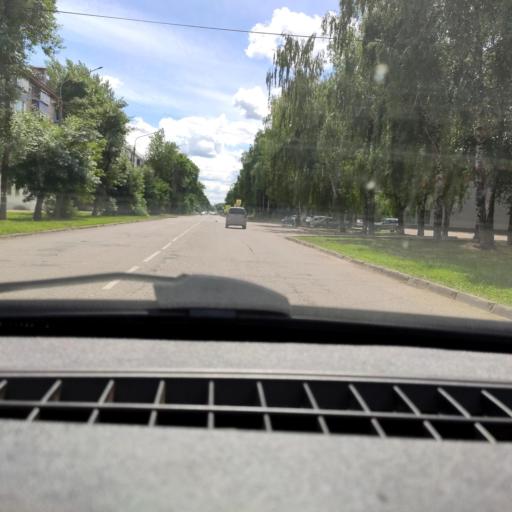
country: RU
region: Bashkortostan
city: Sterlitamak
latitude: 53.6430
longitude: 55.9337
